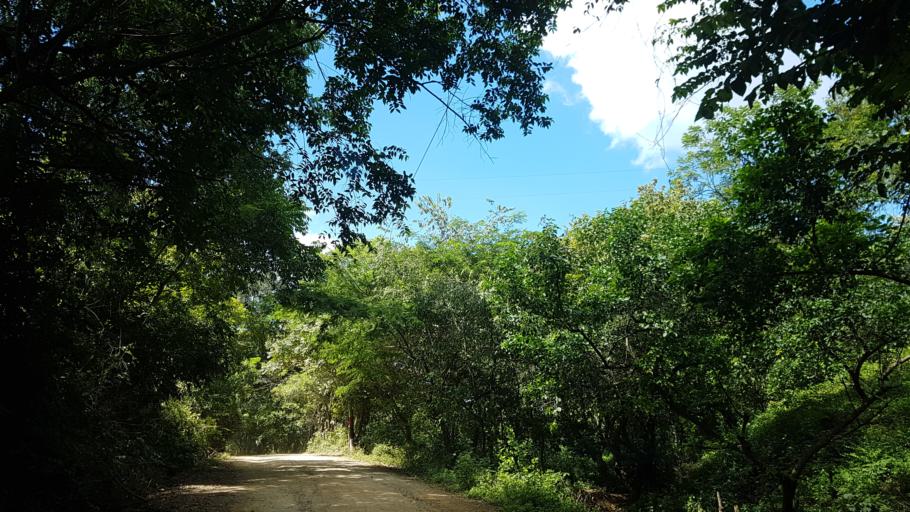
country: HN
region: El Paraiso
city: Oropoli
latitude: 13.7363
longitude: -86.6966
